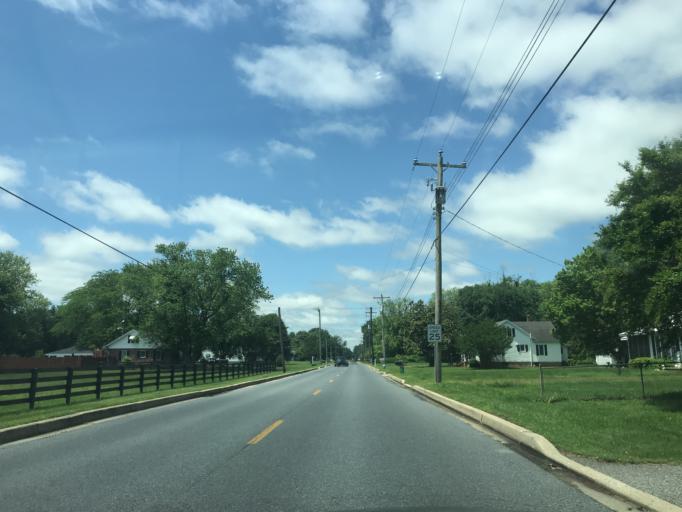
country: US
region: Maryland
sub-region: Caroline County
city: Federalsburg
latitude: 38.6906
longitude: -75.7826
